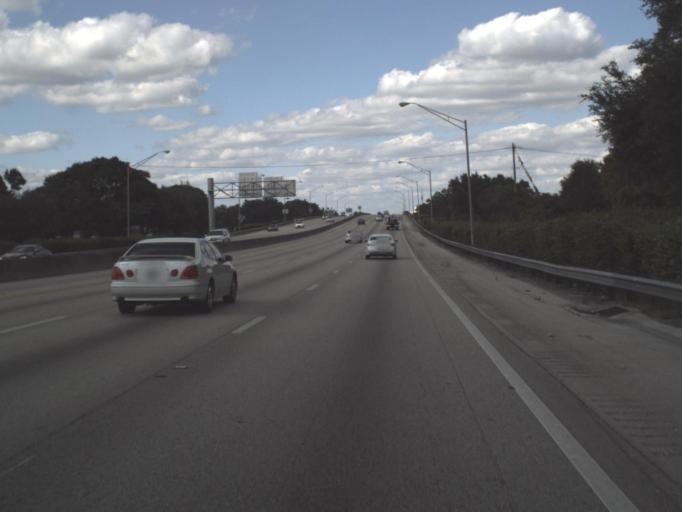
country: US
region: Florida
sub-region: Broward County
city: Pembroke Pines
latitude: 26.0203
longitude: -80.2128
